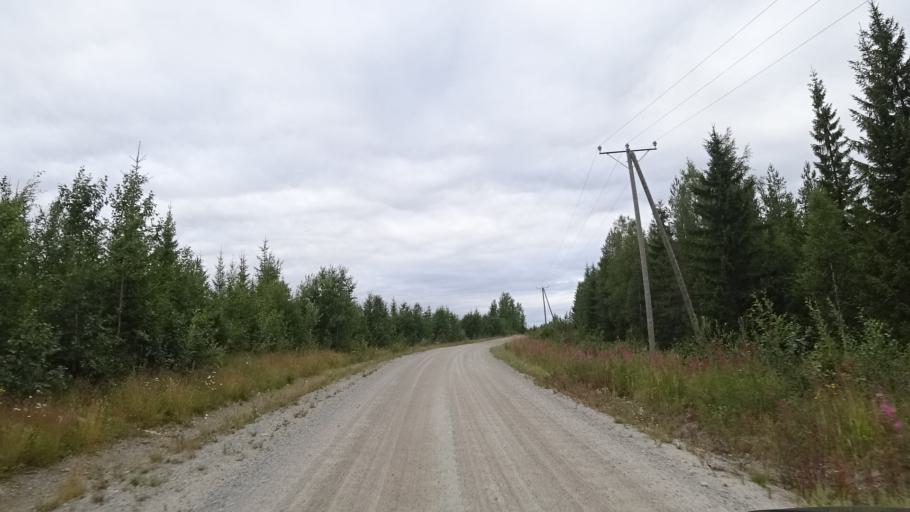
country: FI
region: North Karelia
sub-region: Joensuu
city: Eno
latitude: 63.1609
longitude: 30.5802
